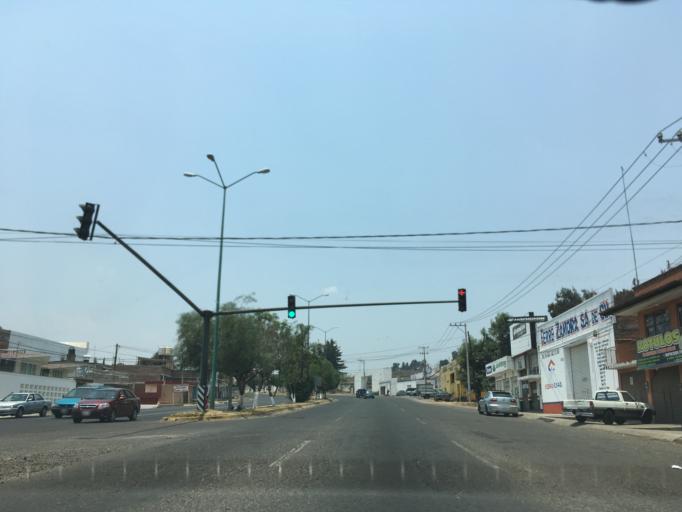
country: MX
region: Michoacan
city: Patzcuaro
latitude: 19.5224
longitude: -101.6160
